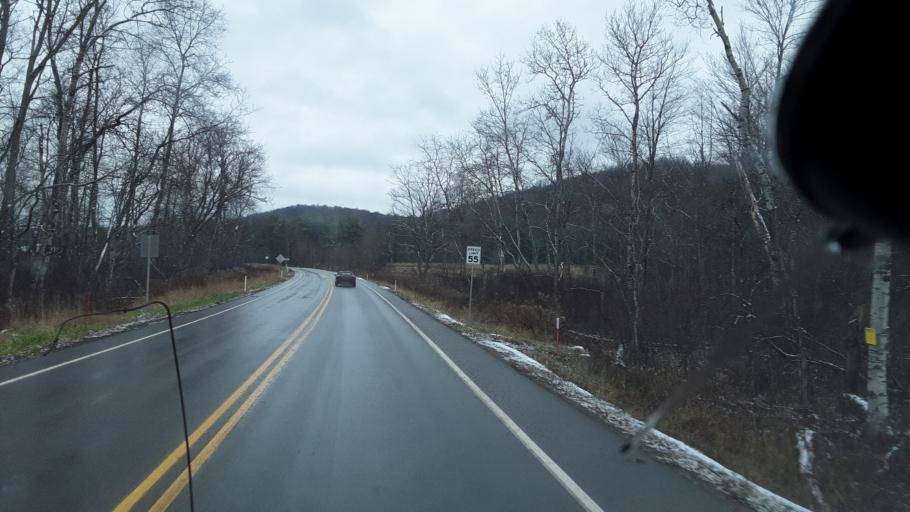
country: US
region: Pennsylvania
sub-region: Potter County
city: Shinglehouse
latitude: 41.9271
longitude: -78.1203
